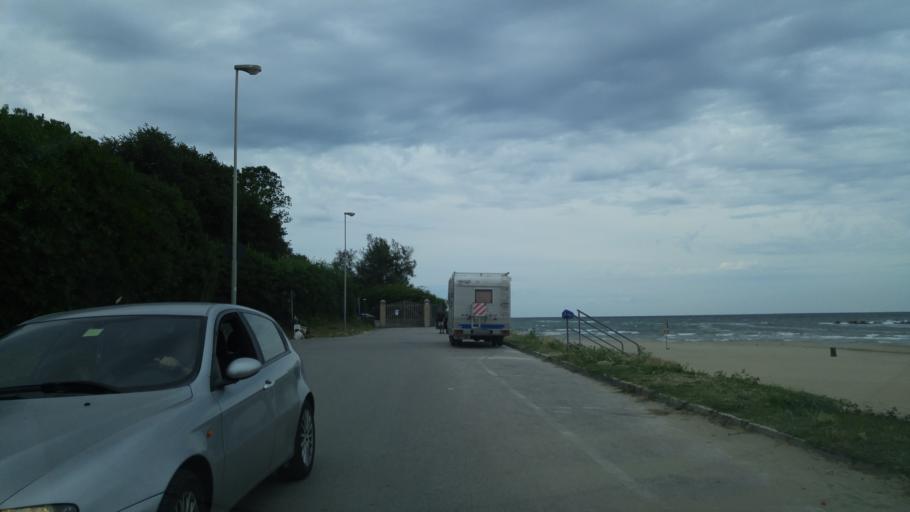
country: IT
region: The Marches
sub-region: Provincia di Pesaro e Urbino
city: Pesaro
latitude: 43.9221
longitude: 12.8944
